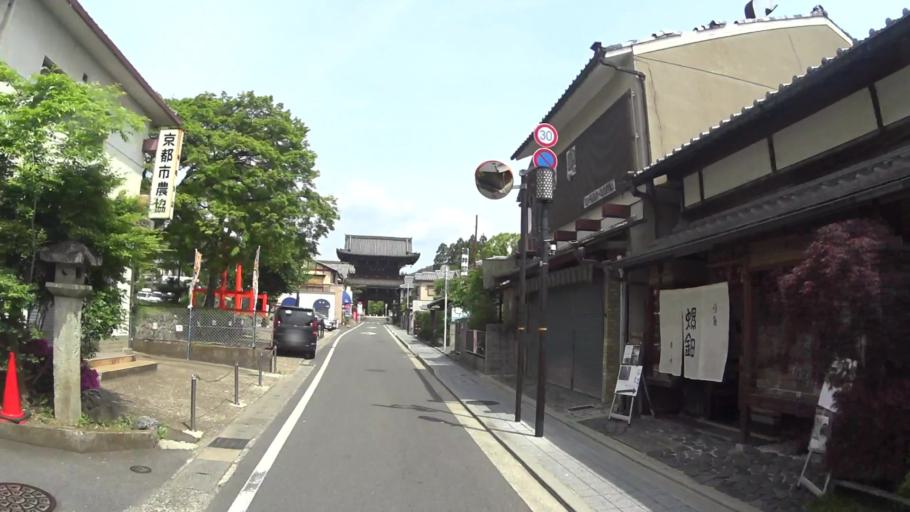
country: JP
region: Kyoto
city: Muko
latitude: 35.0216
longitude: 135.6752
